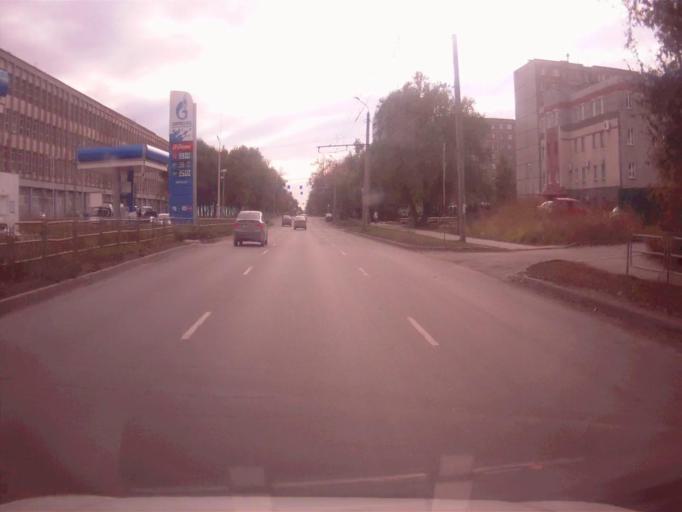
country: RU
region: Chelyabinsk
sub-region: Gorod Chelyabinsk
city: Chelyabinsk
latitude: 55.1245
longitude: 61.4748
